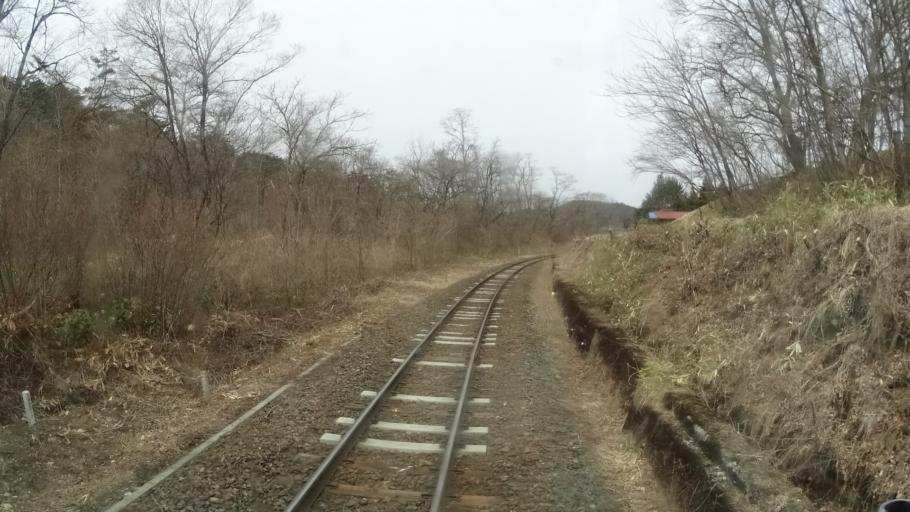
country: JP
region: Iwate
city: Tono
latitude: 39.3271
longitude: 141.3649
